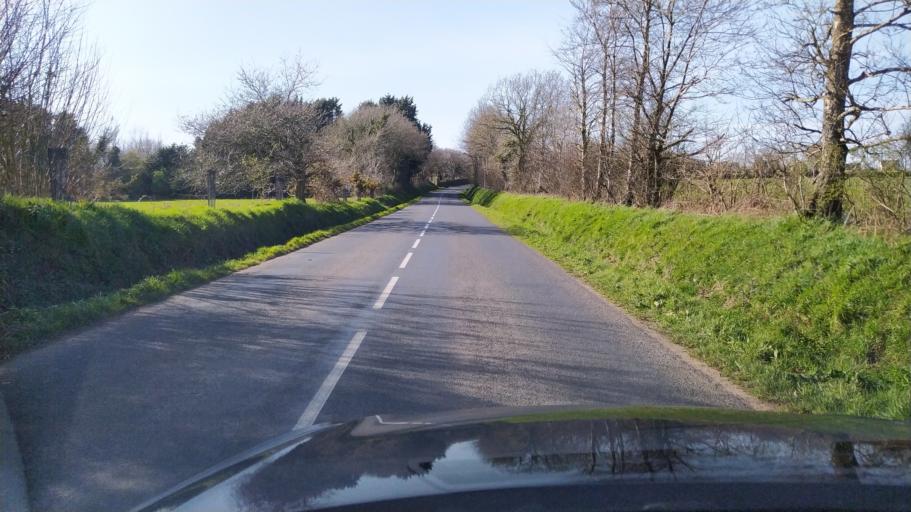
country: FR
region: Brittany
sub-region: Departement du Finistere
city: Lampaul-Guimiliau
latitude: 48.4414
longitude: -3.9984
